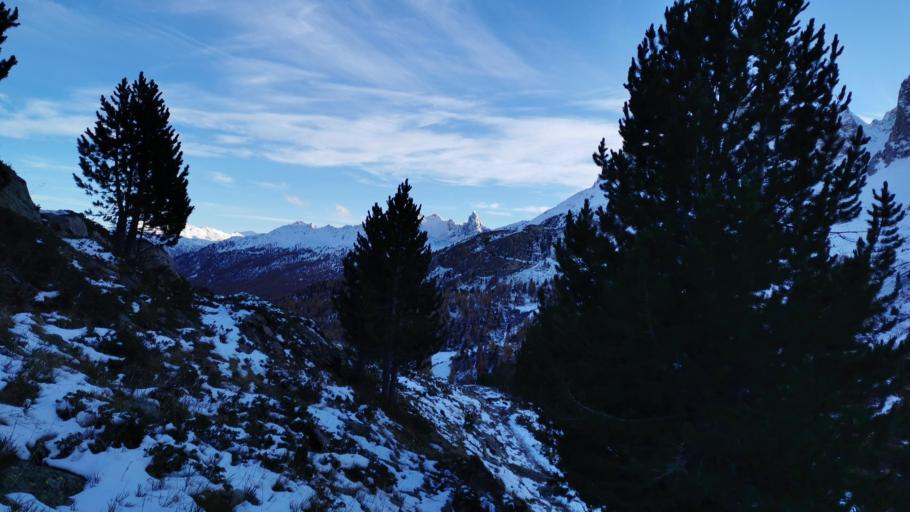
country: FR
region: Provence-Alpes-Cote d'Azur
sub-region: Departement des Hautes-Alpes
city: Le Monetier-les-Bains
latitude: 45.0703
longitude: 6.5169
